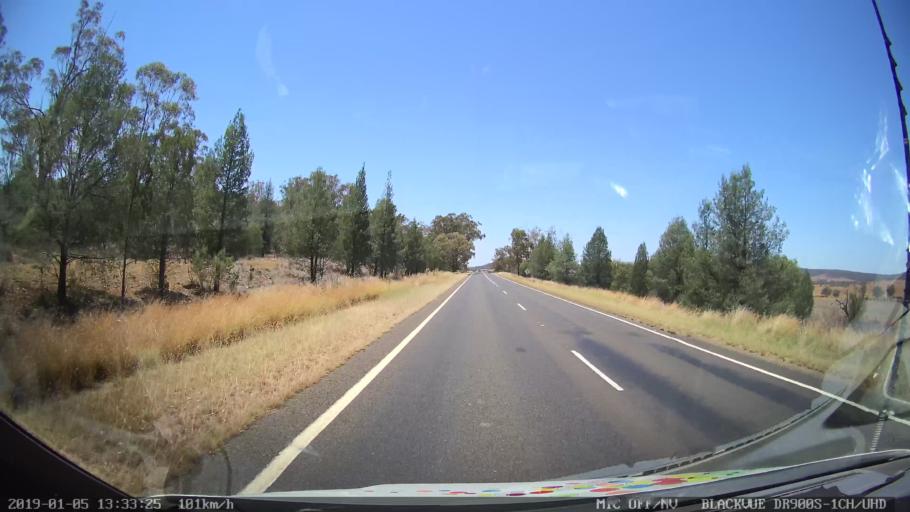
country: AU
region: New South Wales
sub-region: Gunnedah
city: Gunnedah
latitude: -31.0008
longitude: 150.1161
